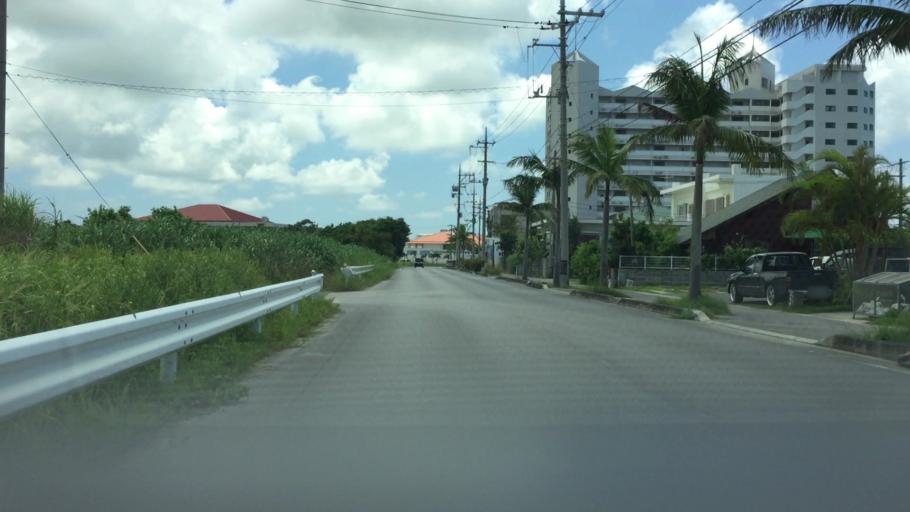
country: JP
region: Okinawa
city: Ishigaki
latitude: 24.3558
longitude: 124.1342
